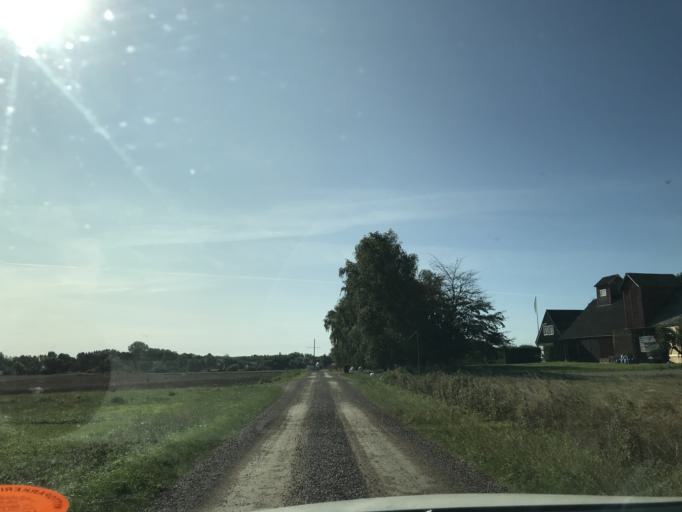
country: SE
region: Skane
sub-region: Landskrona
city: Asmundtorp
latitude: 55.8947
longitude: 12.9488
